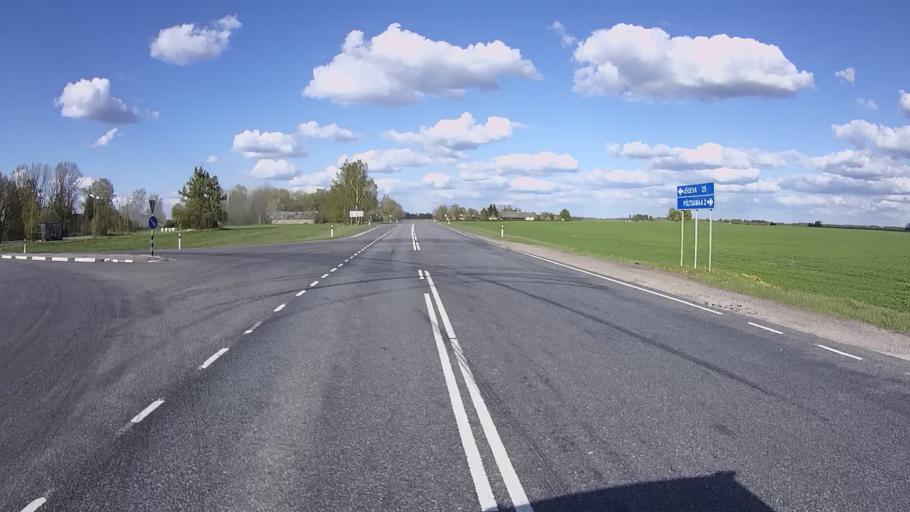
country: EE
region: Jogevamaa
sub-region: Poltsamaa linn
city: Poltsamaa
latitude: 58.6690
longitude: 25.9948
